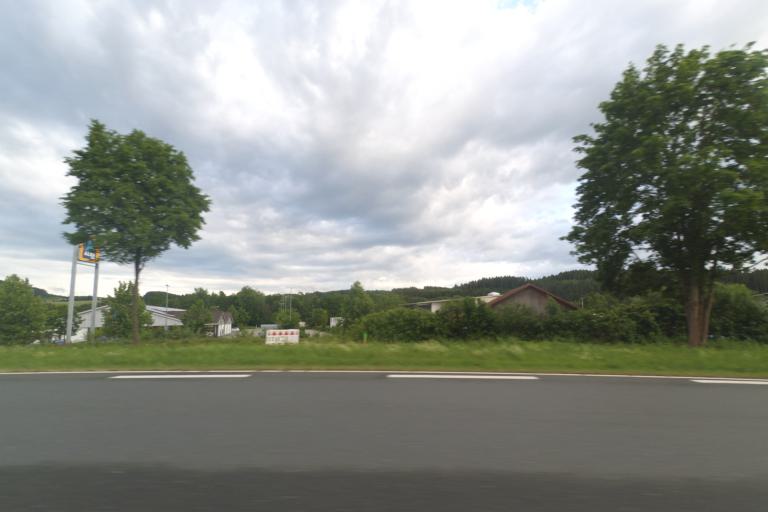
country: DE
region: Bavaria
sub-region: Upper Franconia
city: Kronach
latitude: 50.2328
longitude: 11.3484
